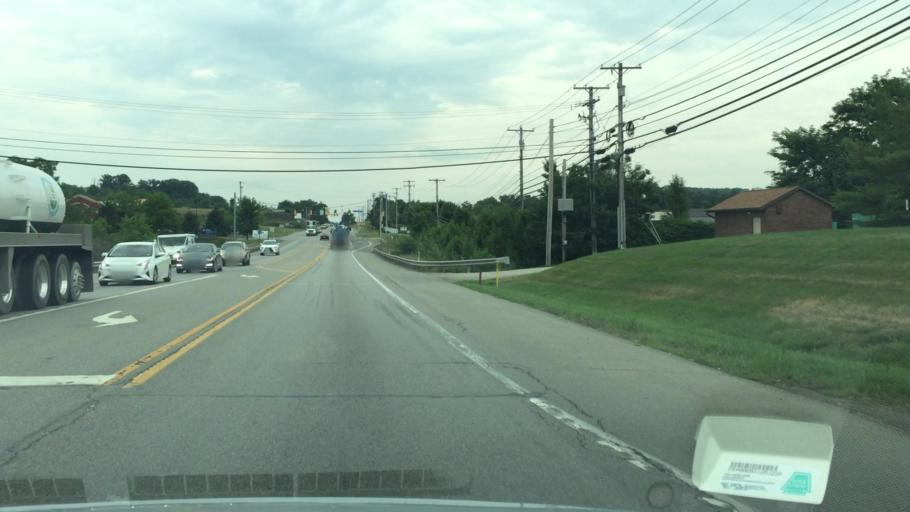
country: US
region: Pennsylvania
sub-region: Butler County
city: Seven Fields
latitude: 40.6871
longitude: -80.0586
